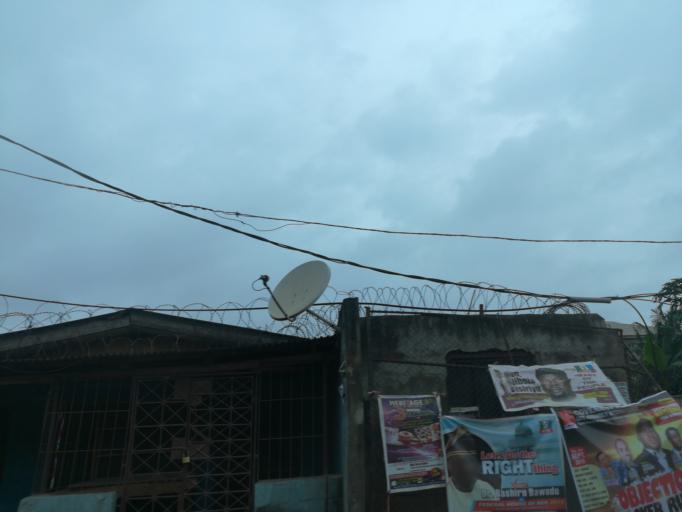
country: NG
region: Lagos
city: Oshodi
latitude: 6.5675
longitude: 3.3423
